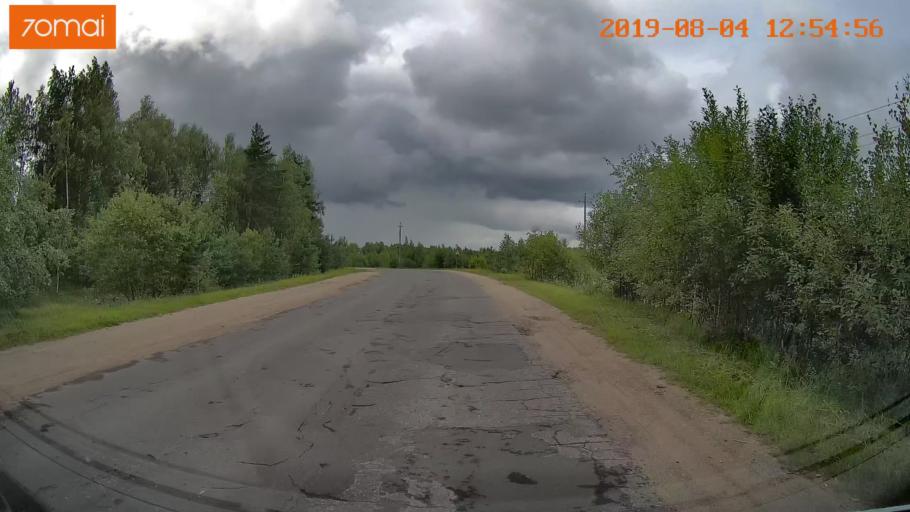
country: RU
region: Ivanovo
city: Novo-Talitsy
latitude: 57.0464
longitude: 40.8528
